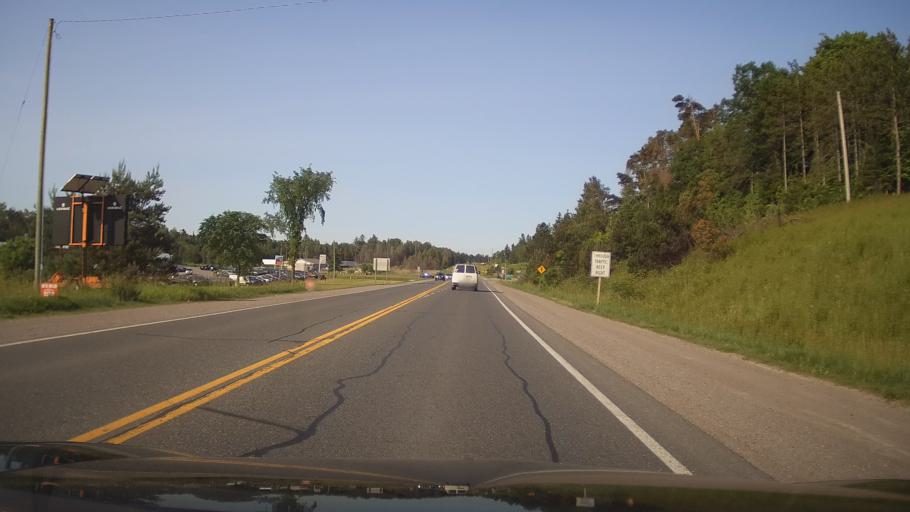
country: CA
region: Ontario
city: Peterborough
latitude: 44.3736
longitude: -77.9887
